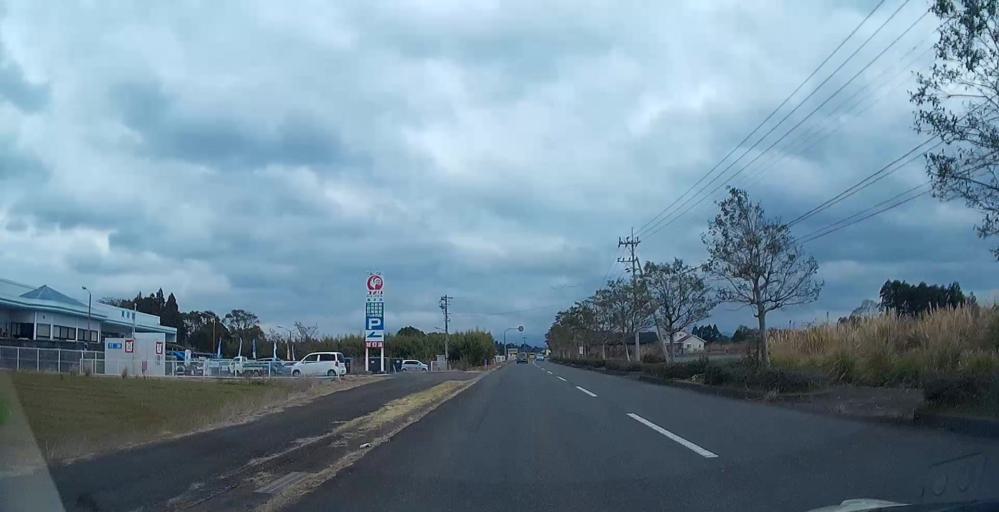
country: JP
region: Kagoshima
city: Akune
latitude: 32.0758
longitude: 130.2099
